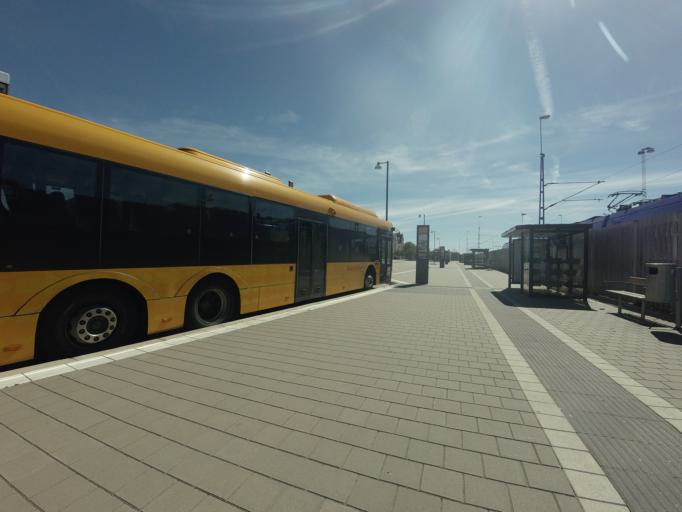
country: SE
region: Skane
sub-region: Trelleborgs Kommun
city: Trelleborg
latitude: 55.3716
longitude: 13.1606
